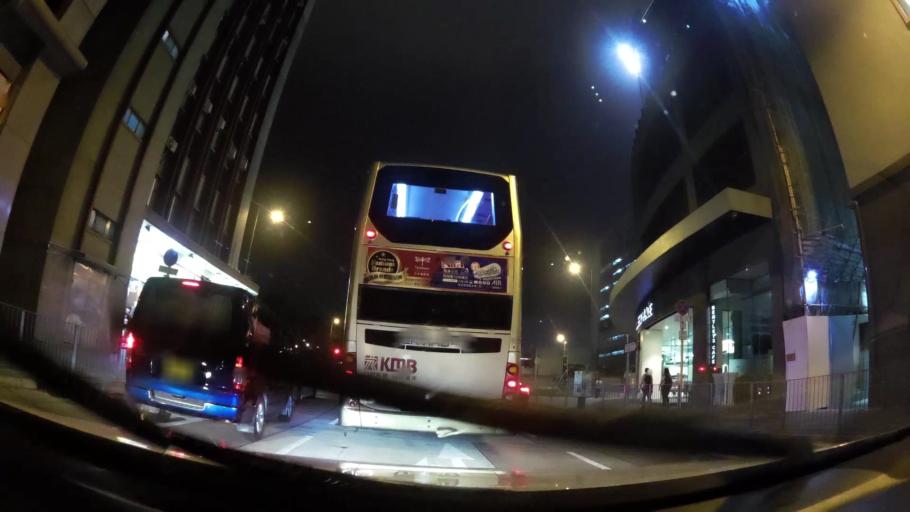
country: HK
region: Kowloon City
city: Kowloon
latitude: 22.3092
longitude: 114.2229
